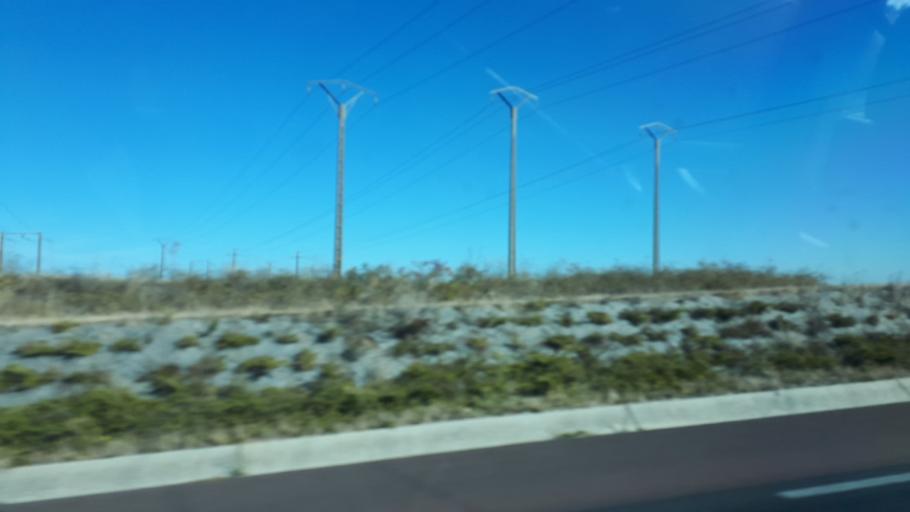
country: FR
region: Centre
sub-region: Departement d'Eure-et-Loir
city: Chateaudun
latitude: 48.0594
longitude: 1.3395
